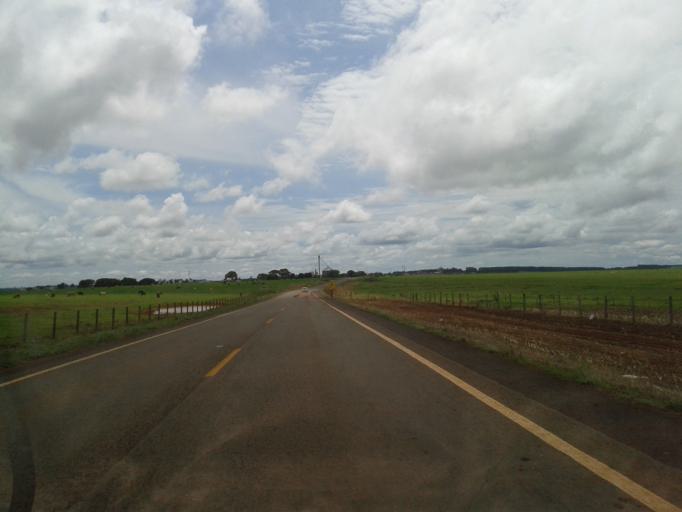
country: BR
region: Goias
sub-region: Buriti Alegre
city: Buriti Alegre
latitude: -18.1364
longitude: -49.0171
